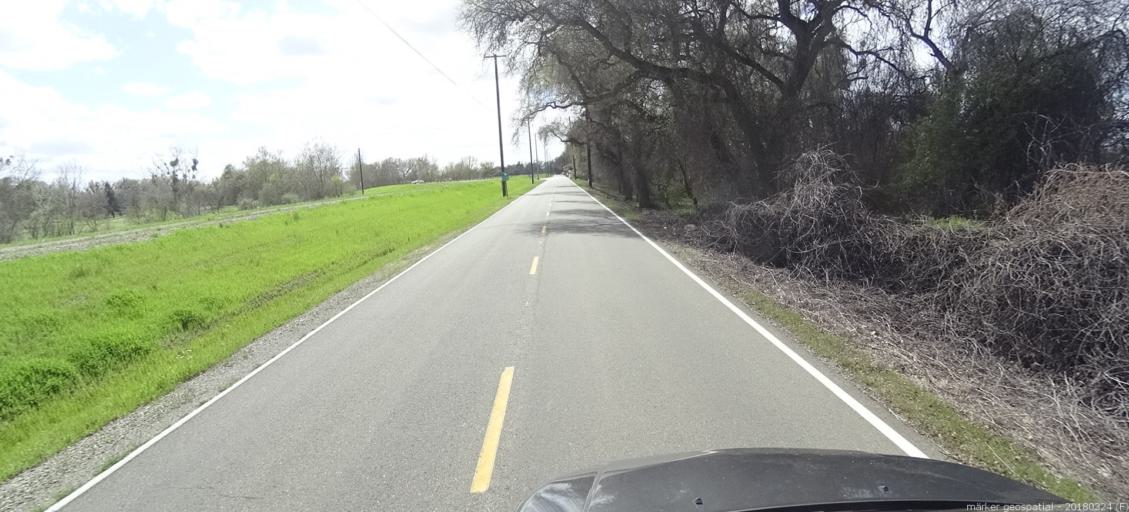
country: US
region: California
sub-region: Yolo County
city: West Sacramento
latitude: 38.7024
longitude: -121.6212
